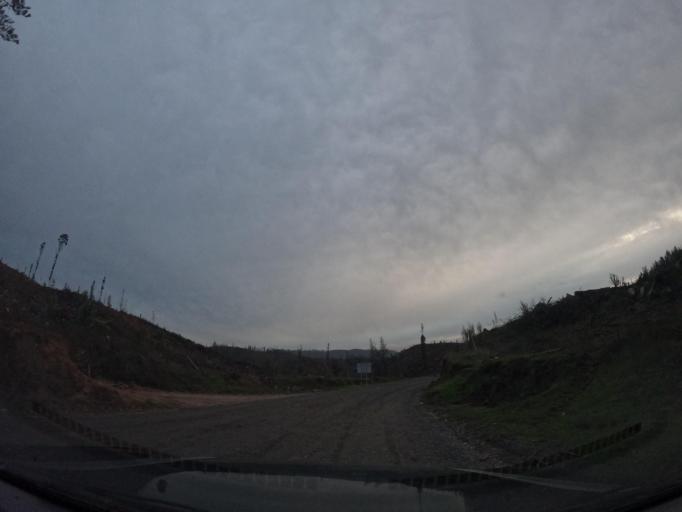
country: CL
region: Biobio
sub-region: Provincia de Concepcion
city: Chiguayante
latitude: -37.0123
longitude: -72.8962
